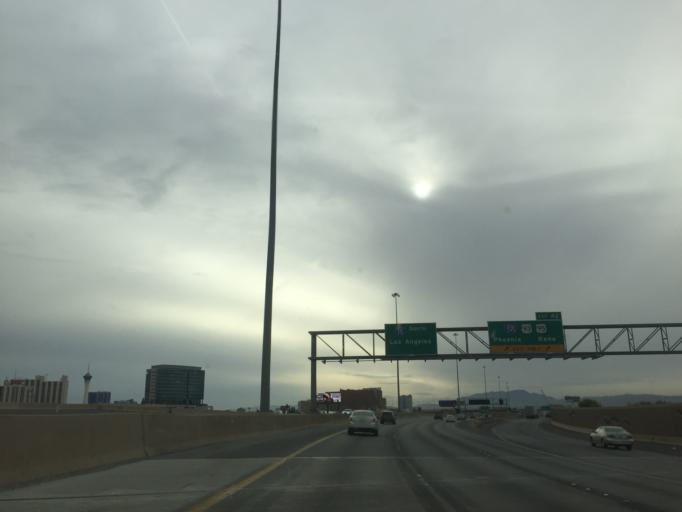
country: US
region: Nevada
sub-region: Clark County
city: Las Vegas
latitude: 36.1811
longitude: -115.1450
